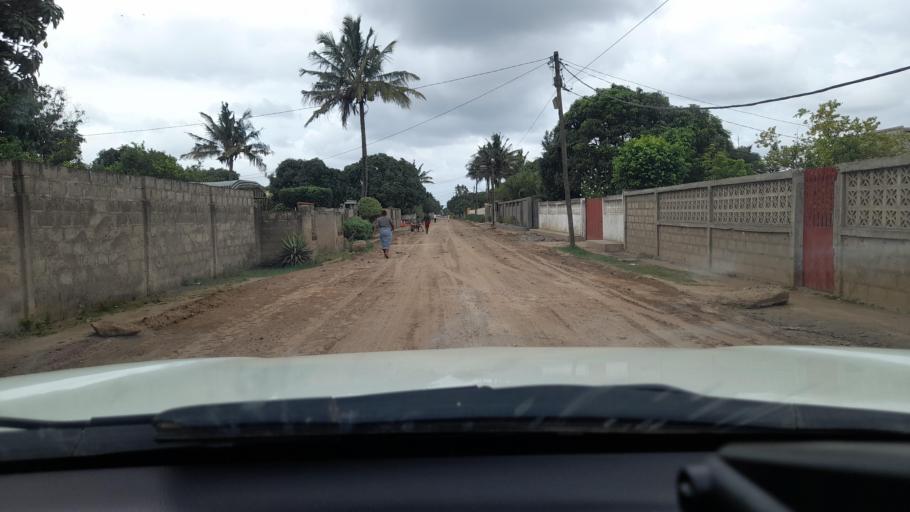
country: MZ
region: Maputo
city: Matola
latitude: -25.9005
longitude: 32.4839
